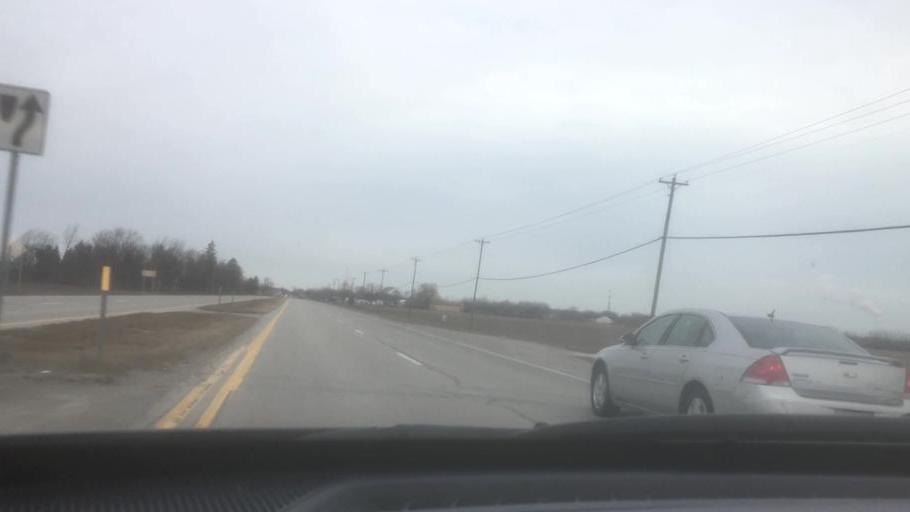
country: US
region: Michigan
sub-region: Bay County
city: Essexville
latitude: 43.5668
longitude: -83.8455
